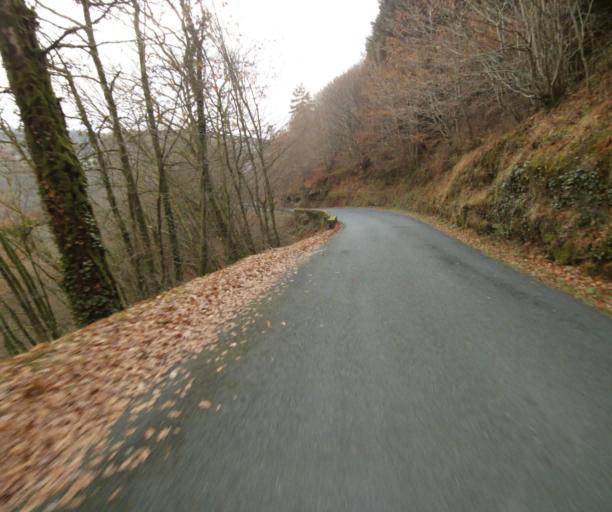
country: FR
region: Limousin
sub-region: Departement de la Correze
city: Chameyrat
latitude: 45.2242
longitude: 1.7031
